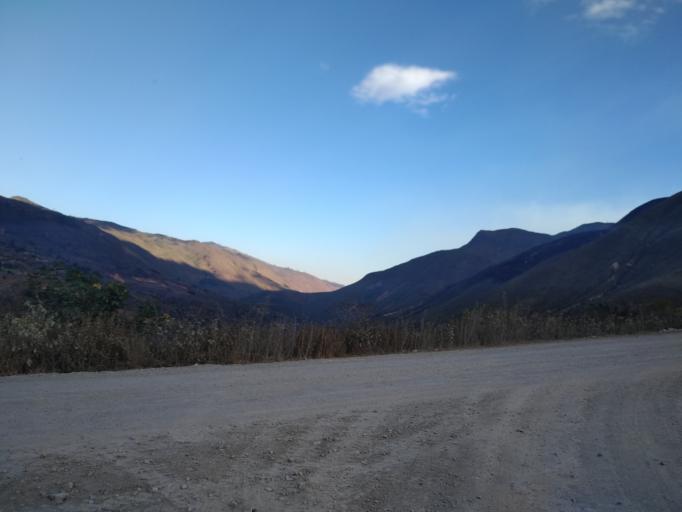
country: PE
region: Amazonas
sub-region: Provincia de Luya
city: Tingo
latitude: -6.3757
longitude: -77.9095
